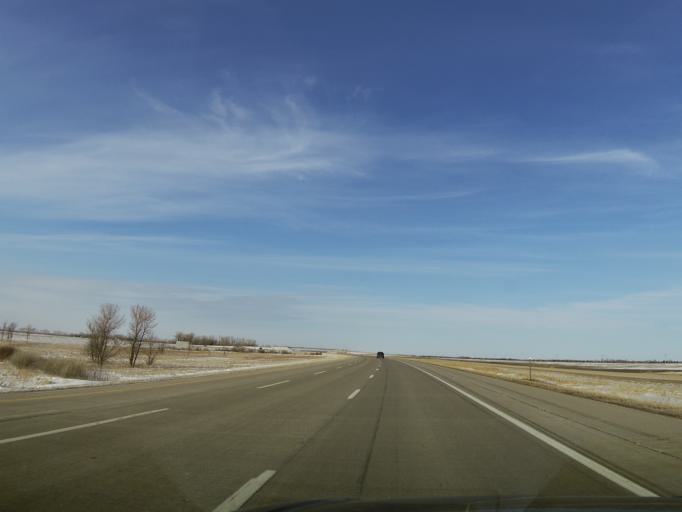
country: US
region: North Dakota
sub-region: Walsh County
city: Grafton
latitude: 48.4623
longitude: -97.1907
